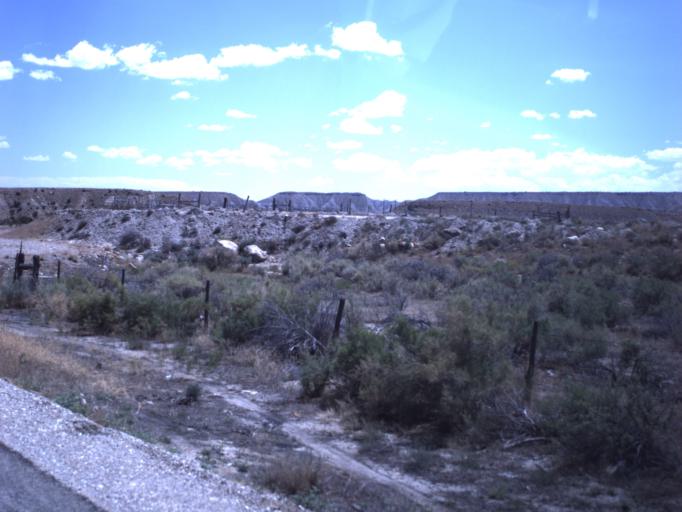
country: US
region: Utah
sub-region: Emery County
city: Orangeville
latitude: 39.2529
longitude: -111.0951
